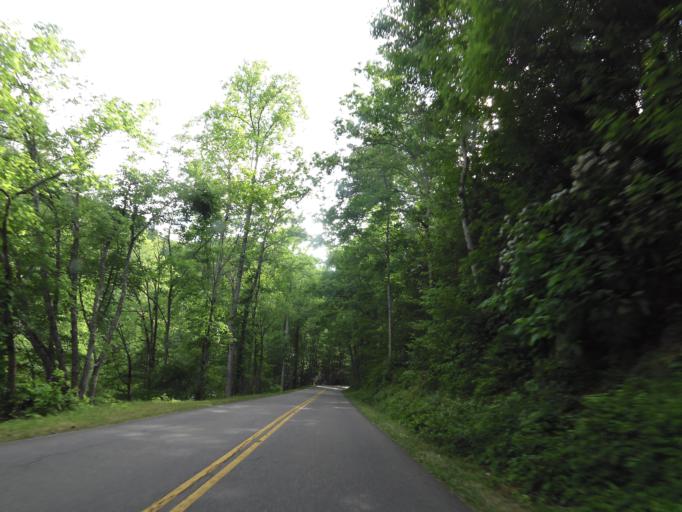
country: US
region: Tennessee
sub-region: Sevier County
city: Gatlinburg
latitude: 35.6635
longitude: -83.6186
